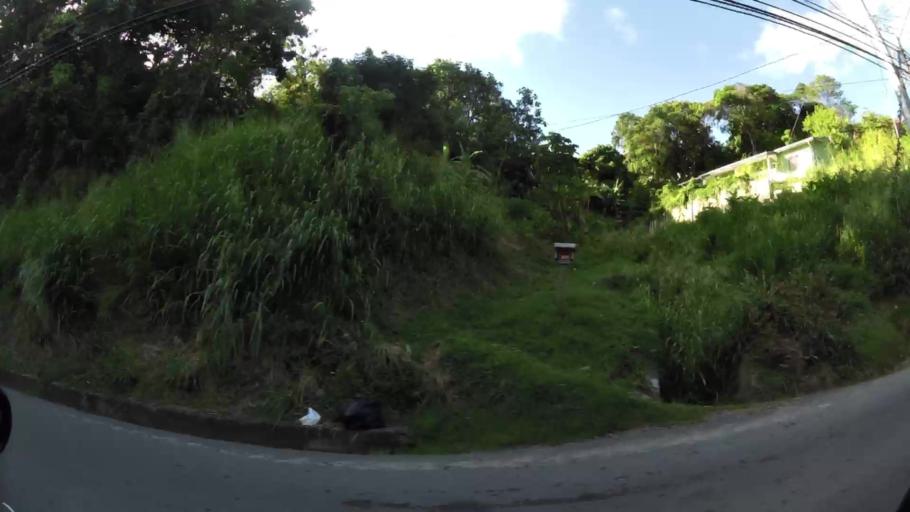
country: TT
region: Eastern Tobago
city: Roxborough
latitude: 11.2208
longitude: -60.6147
